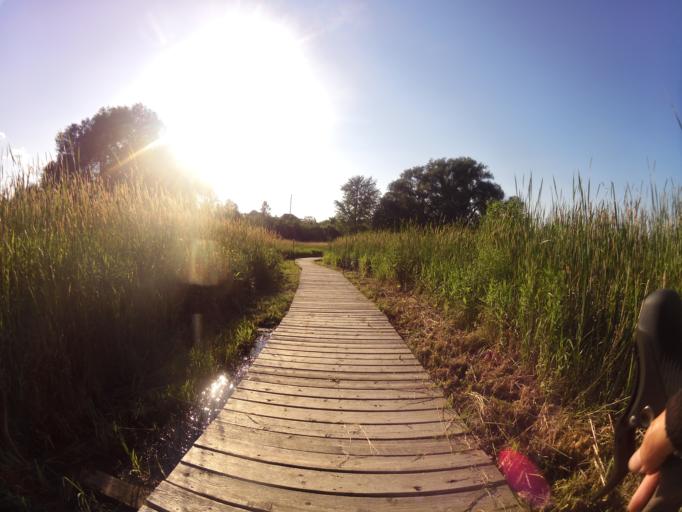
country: CA
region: Ontario
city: Bells Corners
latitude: 45.2746
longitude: -75.7026
